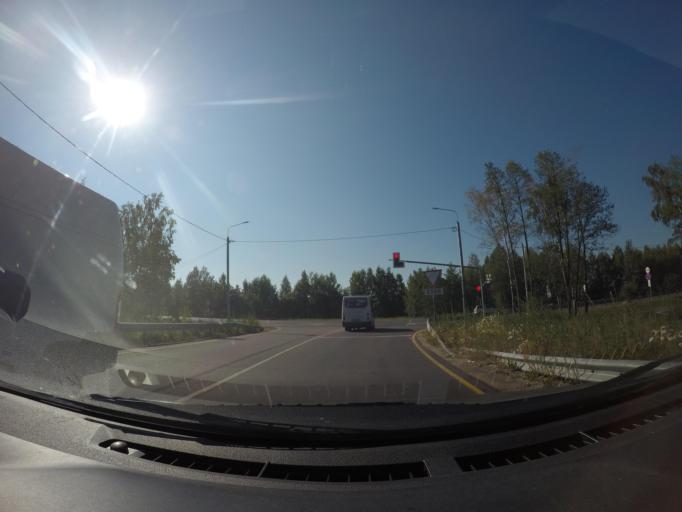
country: RU
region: Moskovskaya
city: Fryazevo
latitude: 55.7352
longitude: 38.4347
